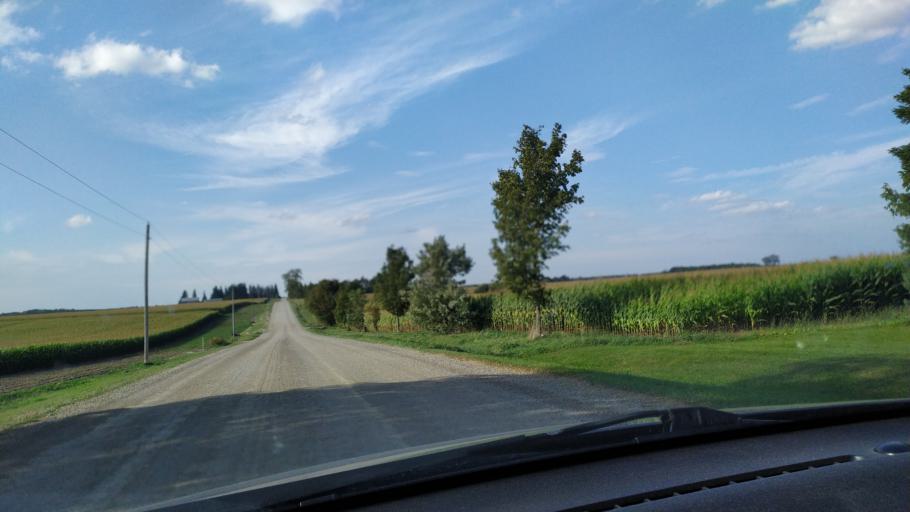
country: CA
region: Ontario
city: Stratford
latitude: 43.2726
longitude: -80.9409
